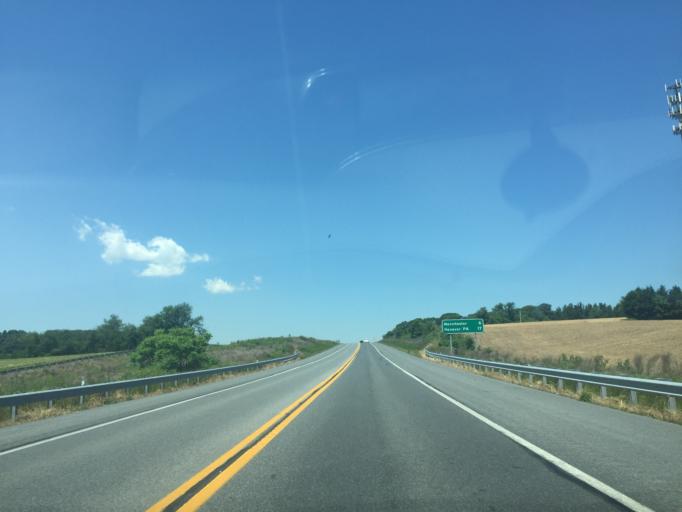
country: US
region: Maryland
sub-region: Carroll County
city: Hampstead
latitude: 39.5835
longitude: -76.8463
